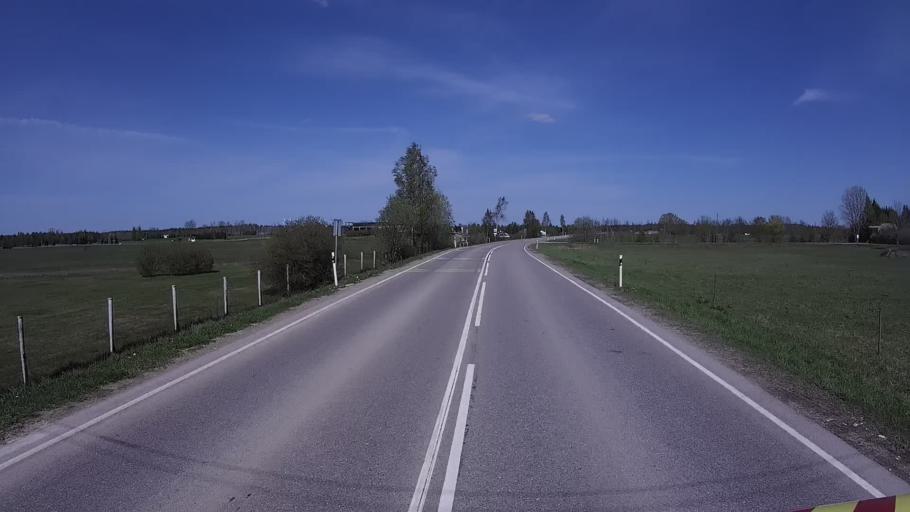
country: EE
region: Harju
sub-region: Keila linn
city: Keila
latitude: 59.3145
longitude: 24.3172
